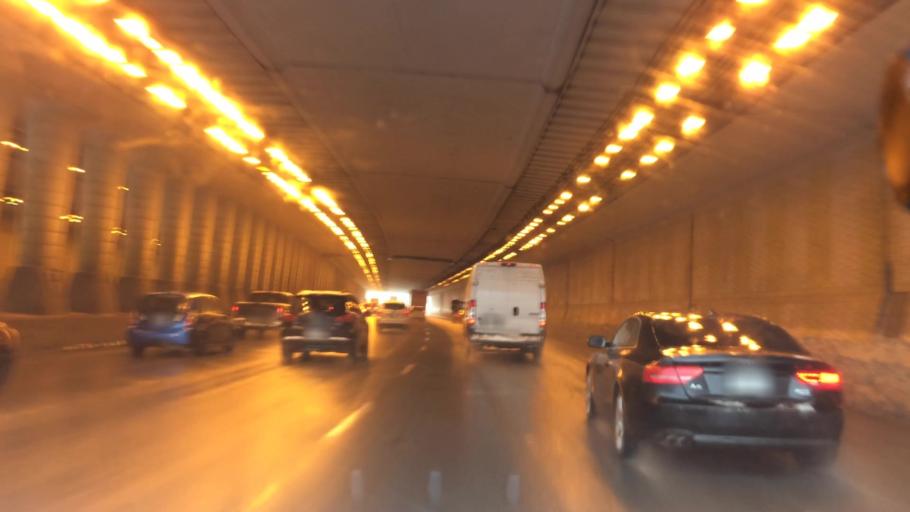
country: CA
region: Quebec
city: Saint-Raymond
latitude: 45.4770
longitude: -73.6185
